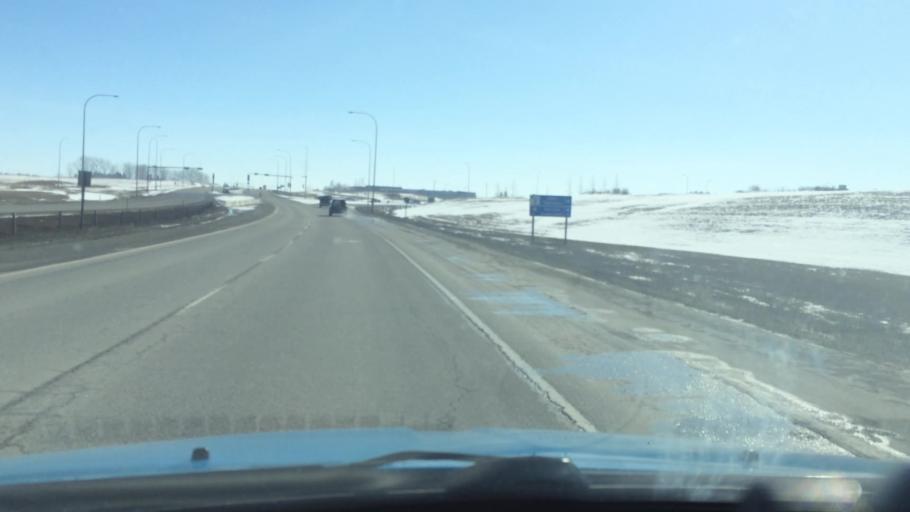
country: CA
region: Alberta
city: Airdrie
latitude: 51.2123
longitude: -113.9945
